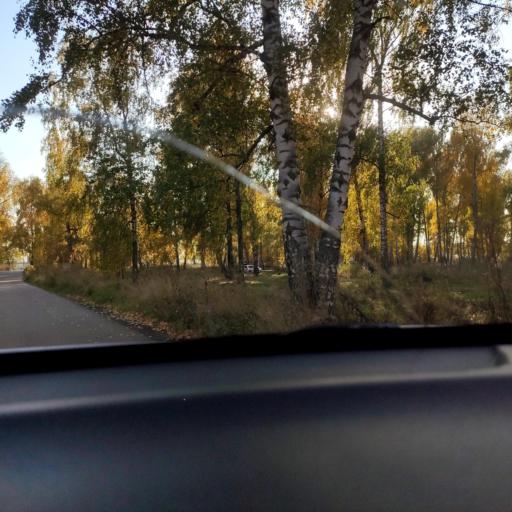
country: RU
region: Tatarstan
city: Stolbishchi
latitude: 55.7097
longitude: 49.1625
